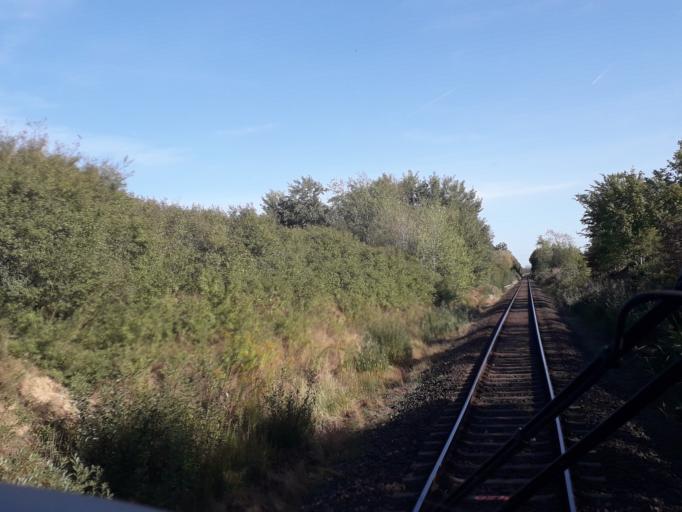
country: DE
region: Brandenburg
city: Velten
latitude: 52.7259
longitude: 13.1081
